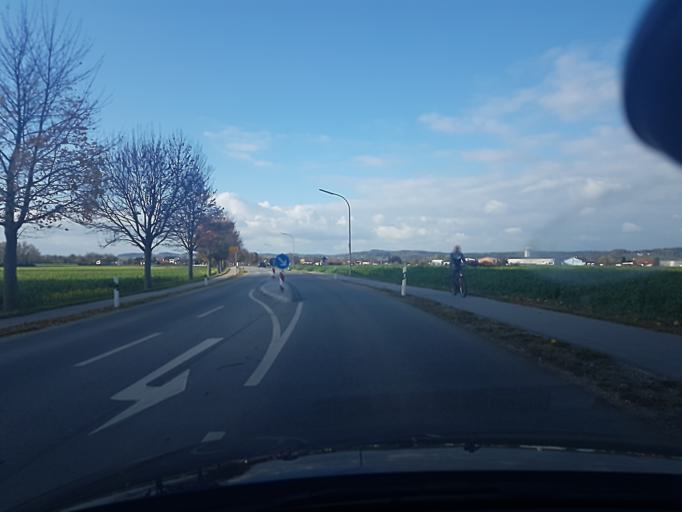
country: DE
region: Bavaria
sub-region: Lower Bavaria
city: Niederaichbach
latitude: 48.6139
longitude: 12.3125
